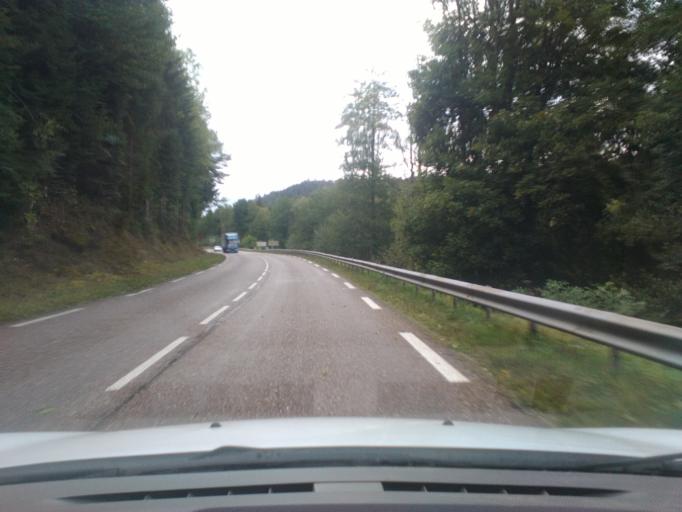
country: FR
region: Lorraine
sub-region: Departement des Vosges
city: Bruyeres
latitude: 48.2608
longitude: 6.7988
